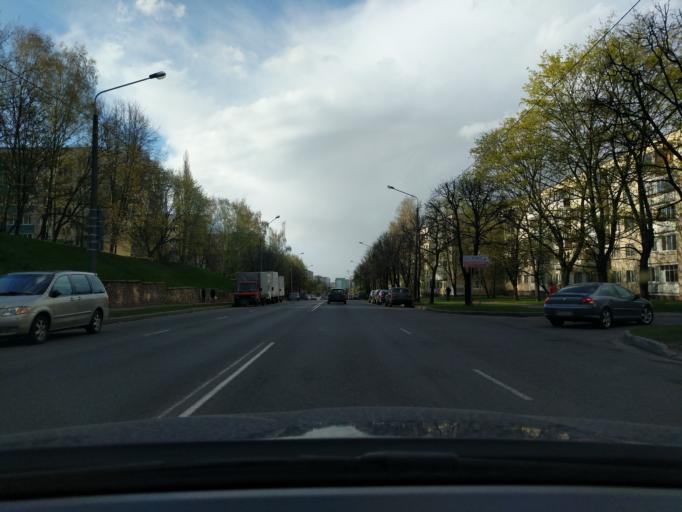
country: BY
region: Minsk
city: Novoye Medvezhino
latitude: 53.9125
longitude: 27.4802
